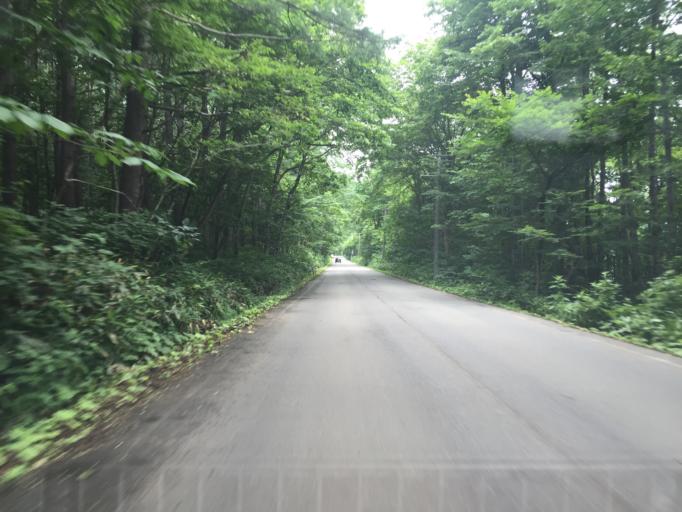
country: JP
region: Fukushima
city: Inawashiro
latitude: 37.7105
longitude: 140.0630
